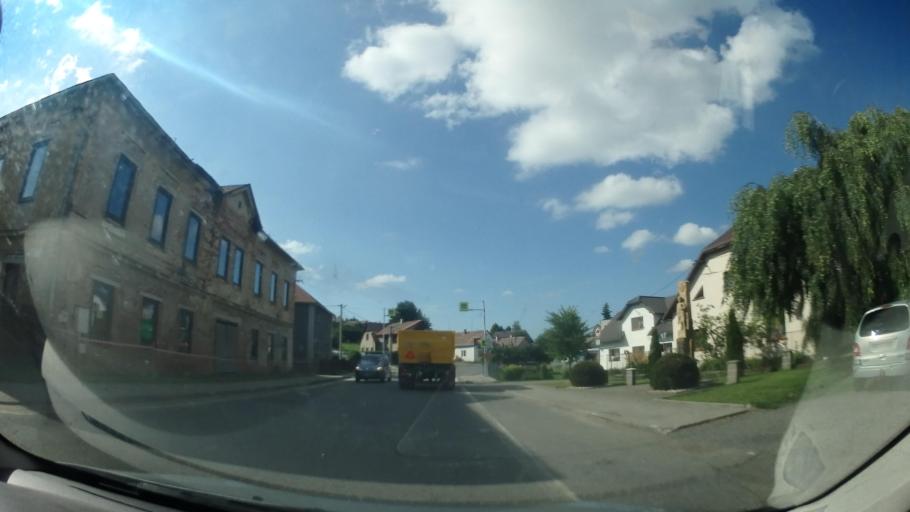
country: CZ
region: Vysocina
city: Heralec
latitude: 49.6900
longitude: 15.9920
